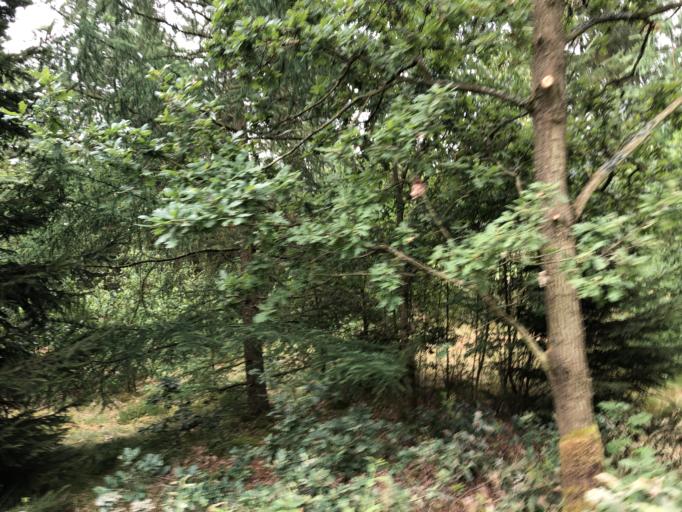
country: DK
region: Central Jutland
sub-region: Holstebro Kommune
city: Ulfborg
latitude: 56.3247
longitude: 8.4270
